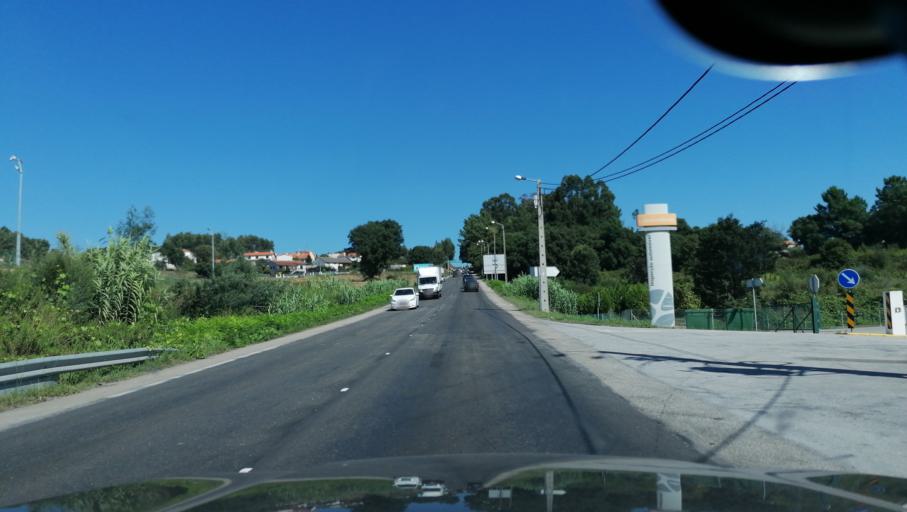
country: PT
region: Aveiro
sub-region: Santa Maria da Feira
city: Feira
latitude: 40.9310
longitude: -8.5234
